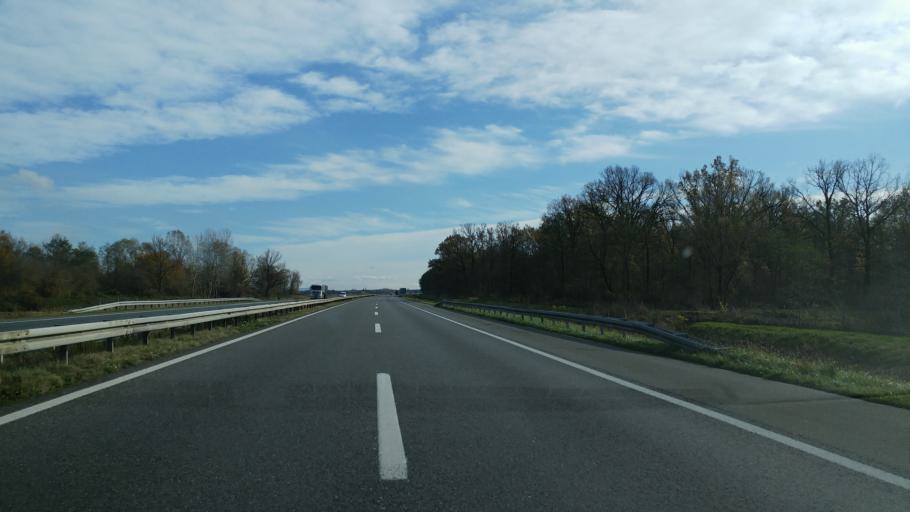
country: HR
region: Sisacko-Moslavacka
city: Repusnica
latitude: 45.4747
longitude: 16.7331
